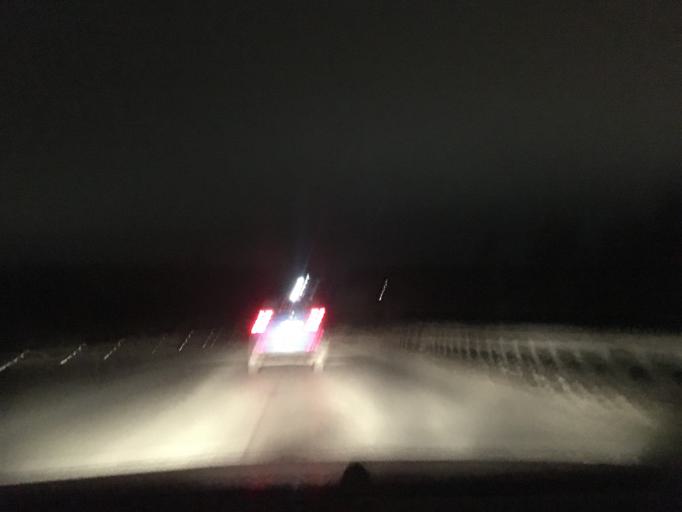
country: RU
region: Tula
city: Mendeleyevskiy
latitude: 54.1264
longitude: 37.5751
